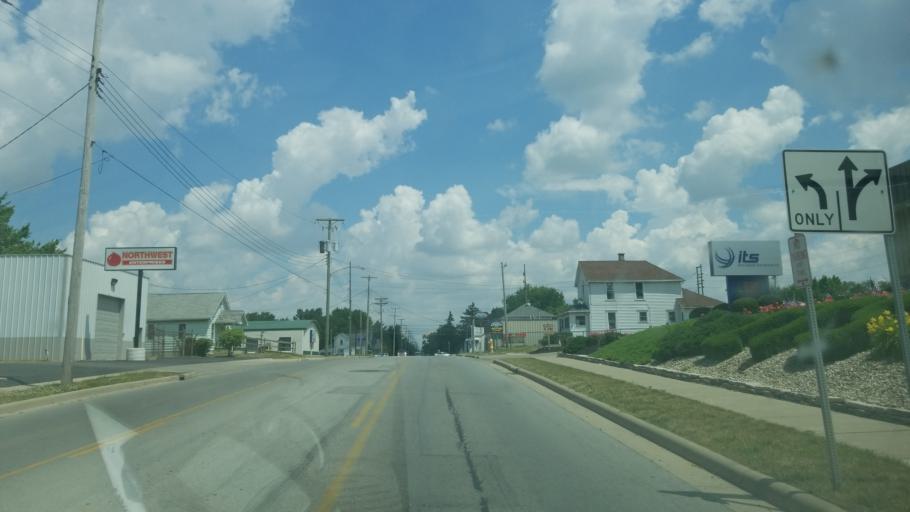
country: US
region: Ohio
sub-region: Allen County
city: Lima
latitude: 40.7247
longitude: -84.1133
